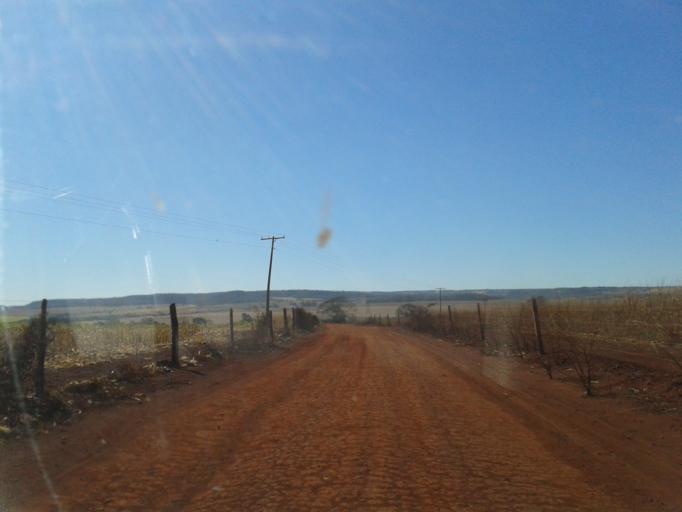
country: BR
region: Minas Gerais
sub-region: Centralina
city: Centralina
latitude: -18.5849
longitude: -49.1364
